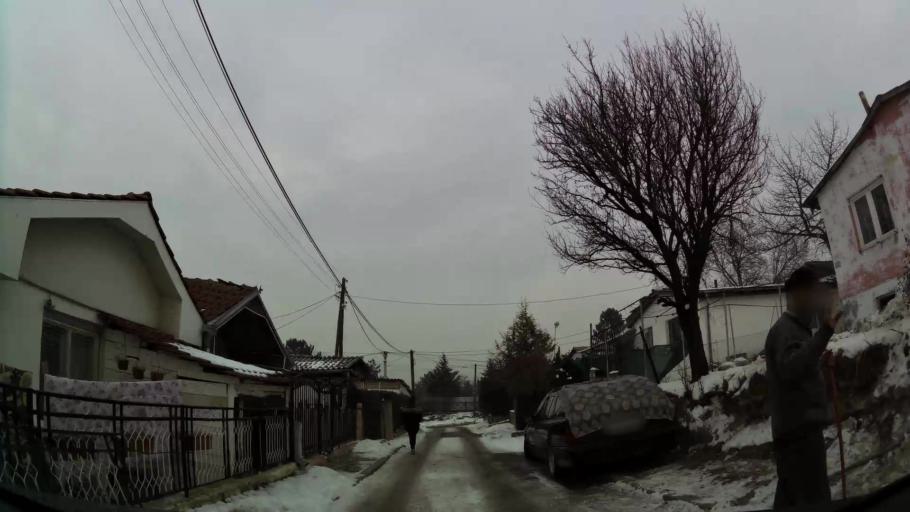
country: MK
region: Suto Orizari
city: Suto Orizare
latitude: 42.0428
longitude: 21.4295
